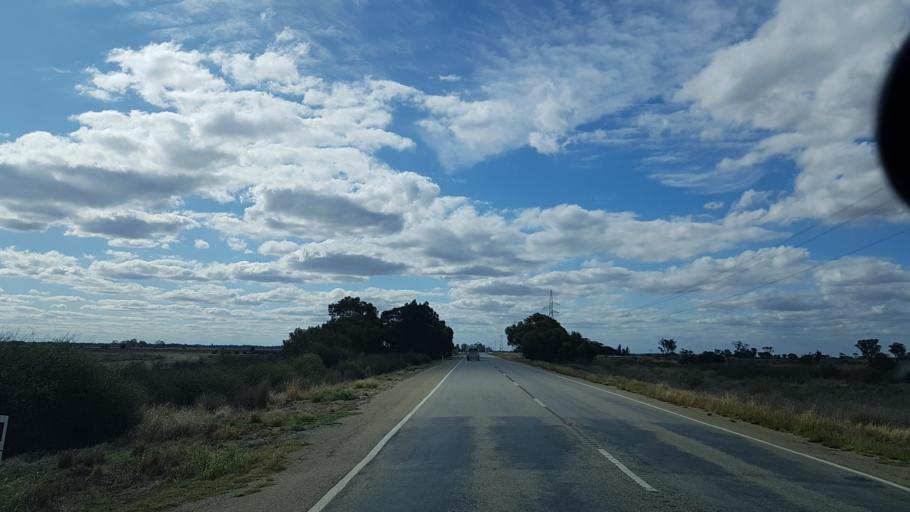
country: AU
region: Victoria
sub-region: Swan Hill
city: Swan Hill
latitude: -35.8681
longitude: 143.9359
